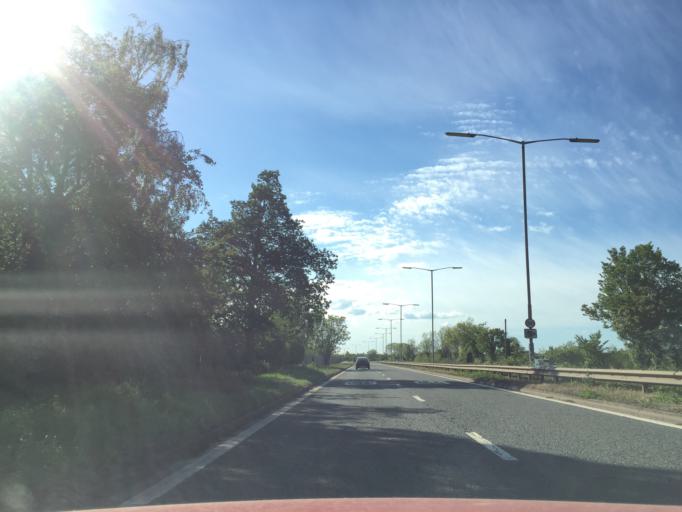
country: GB
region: England
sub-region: Warwickshire
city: Ryton on Dunsmore
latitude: 52.3707
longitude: -1.4473
